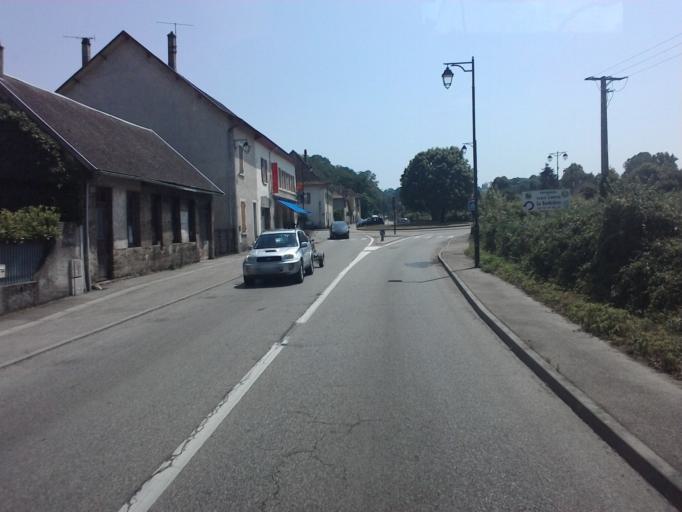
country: FR
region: Rhone-Alpes
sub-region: Departement de l'Isere
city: Corbelin
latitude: 45.6105
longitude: 5.5369
